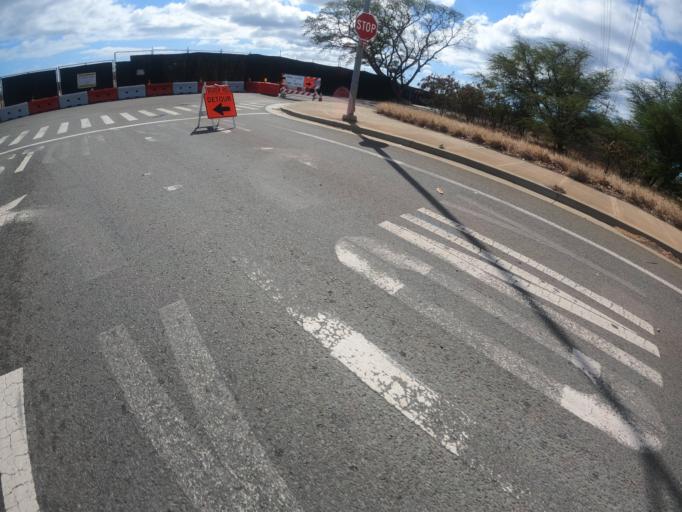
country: US
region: Hawaii
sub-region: Honolulu County
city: Makakilo City
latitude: 21.3255
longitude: -158.0868
